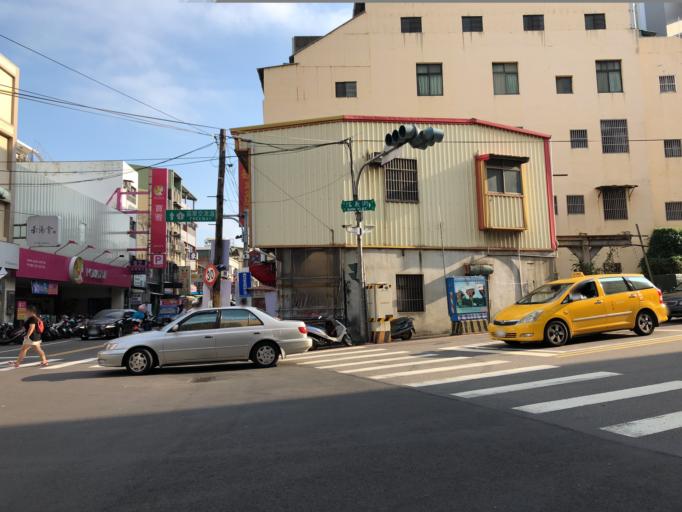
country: TW
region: Taiwan
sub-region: Miaoli
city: Miaoli
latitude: 24.5513
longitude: 120.8159
